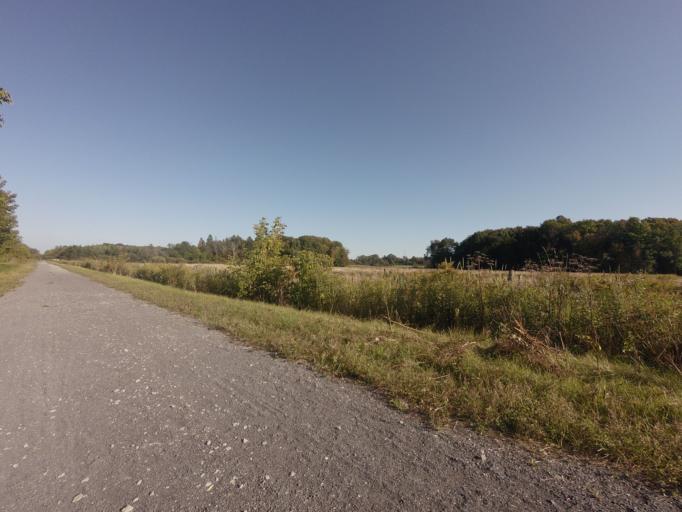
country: CA
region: Ontario
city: Hawkesbury
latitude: 45.5353
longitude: -74.6405
